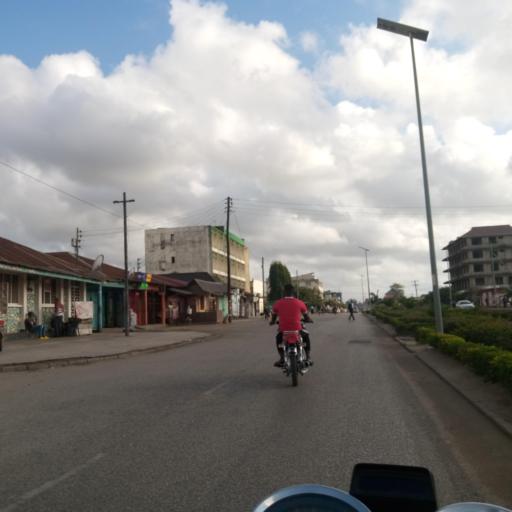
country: TZ
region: Tanga
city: Tanga
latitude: -5.0850
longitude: 39.0973
